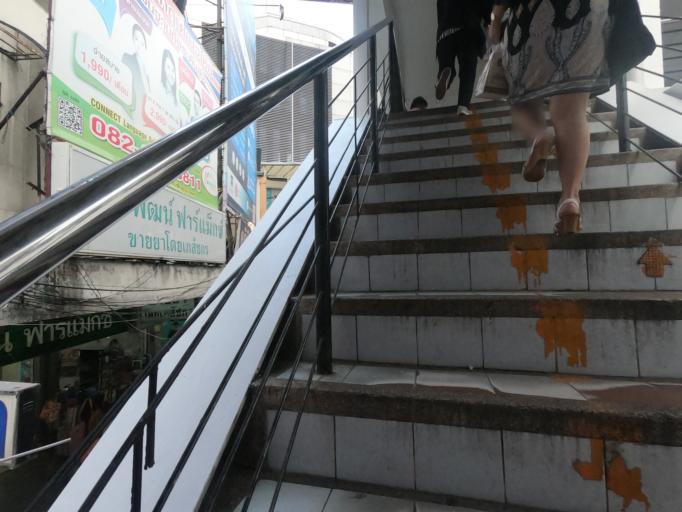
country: TH
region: Bangkok
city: Suan Luang
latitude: 13.7437
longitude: 100.6508
